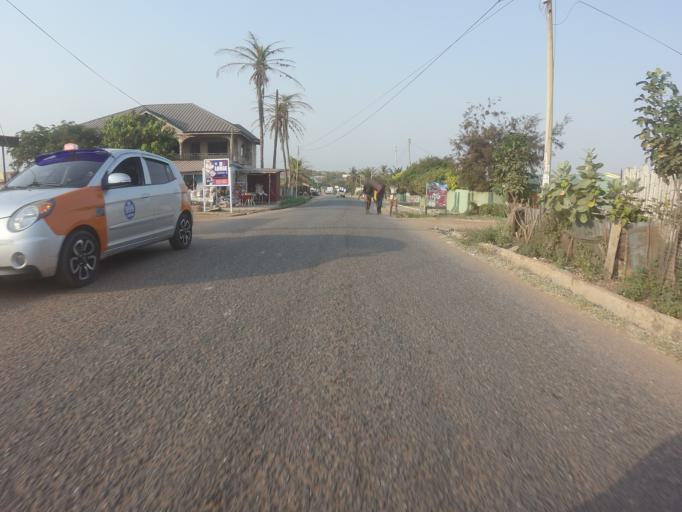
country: GH
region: Greater Accra
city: Nungua
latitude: 5.6153
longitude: -0.0478
